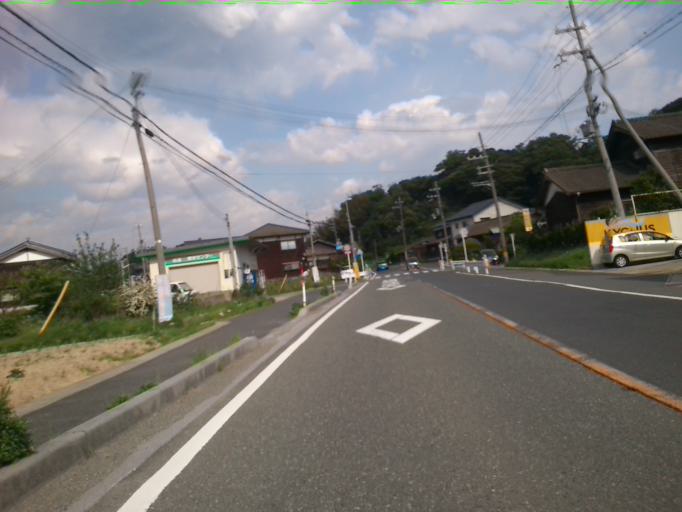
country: JP
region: Kyoto
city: Miyazu
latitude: 35.6823
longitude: 135.0442
